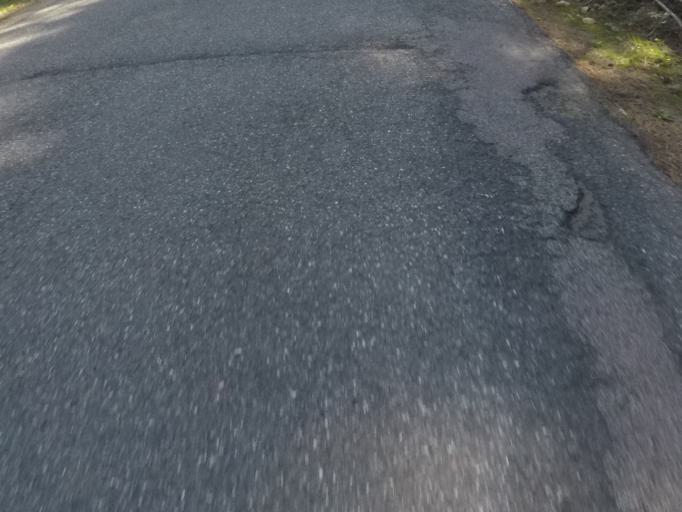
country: FR
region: Corsica
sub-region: Departement de la Haute-Corse
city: Corte
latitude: 42.2901
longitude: 8.9327
